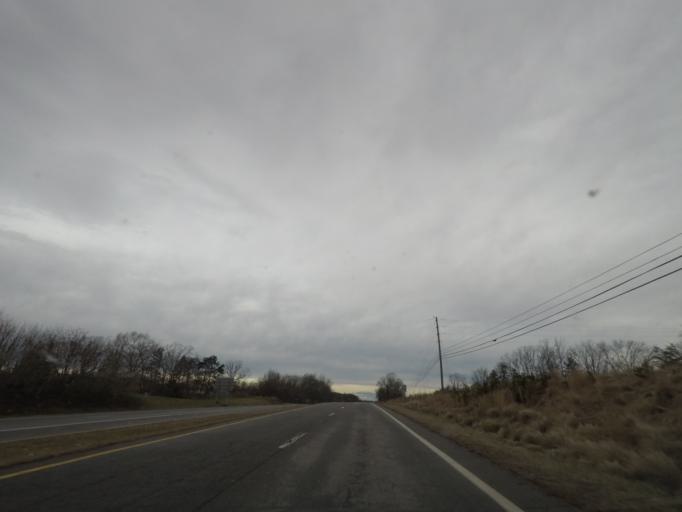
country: US
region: Virginia
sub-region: Pittsylvania County
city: Gretna
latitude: 36.9846
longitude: -79.3545
